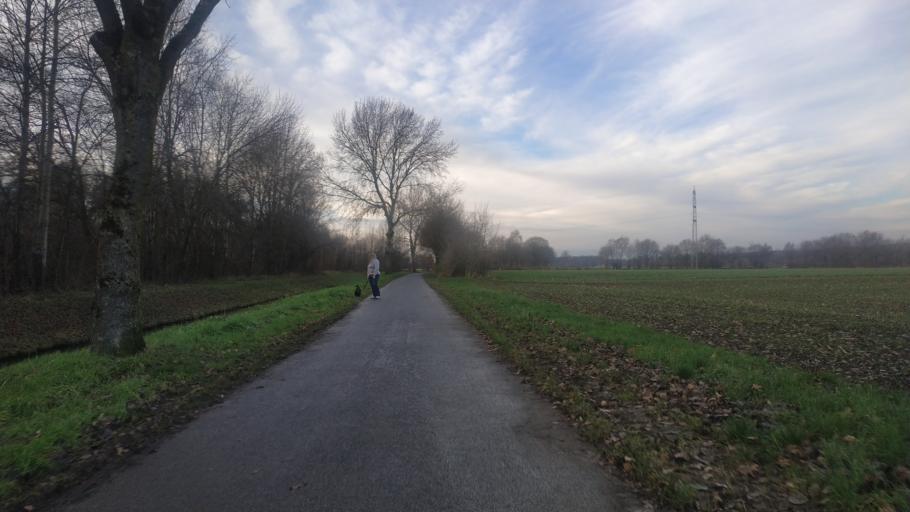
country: DE
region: North Rhine-Westphalia
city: Ibbenburen
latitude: 52.2799
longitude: 7.6844
